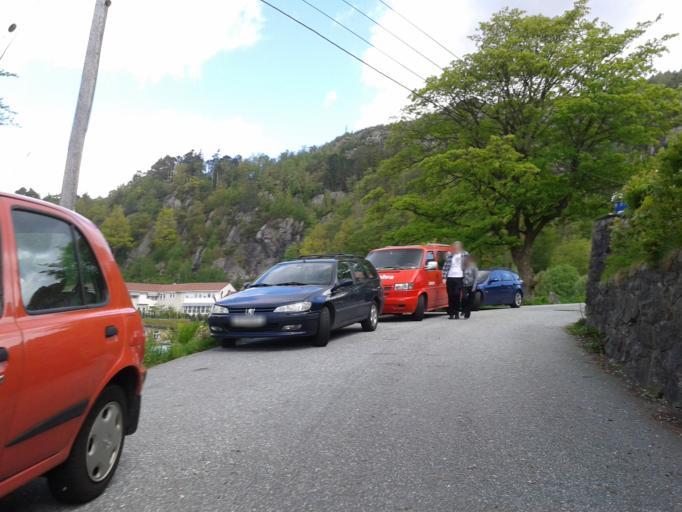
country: NO
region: Hordaland
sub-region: Bergen
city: Bergen
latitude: 60.4177
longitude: 5.3157
